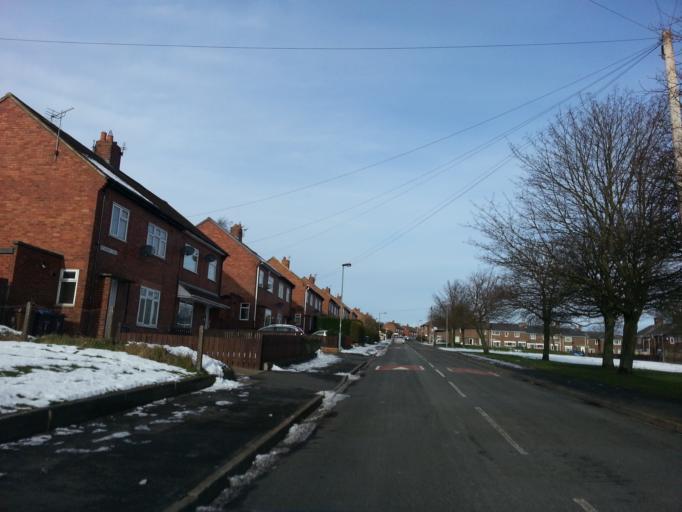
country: GB
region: England
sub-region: County Durham
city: Crook
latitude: 54.7134
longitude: -1.7549
